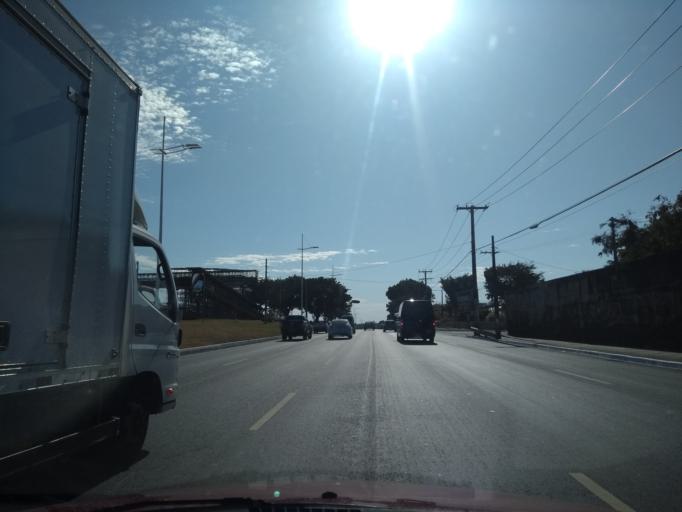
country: BR
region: Bahia
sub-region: Lauro De Freitas
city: Lauro de Freitas
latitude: -12.9226
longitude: -38.3667
